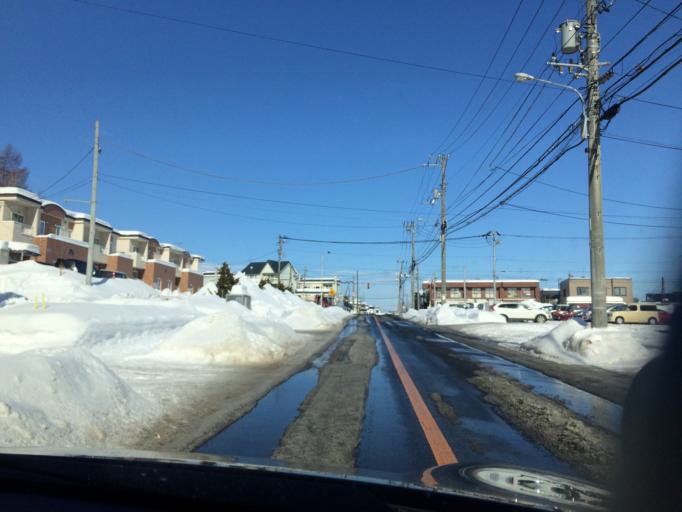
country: JP
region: Hokkaido
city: Kitahiroshima
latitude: 43.0232
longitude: 141.4850
